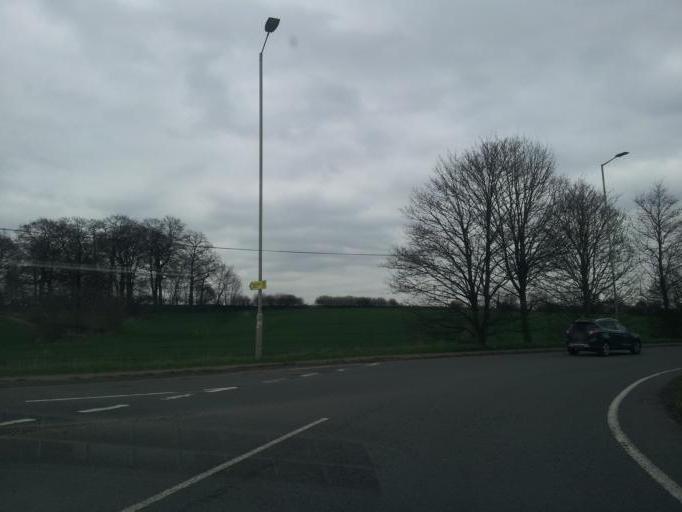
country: GB
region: England
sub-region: Hertfordshire
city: Great Munden
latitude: 51.8973
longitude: 0.0128
